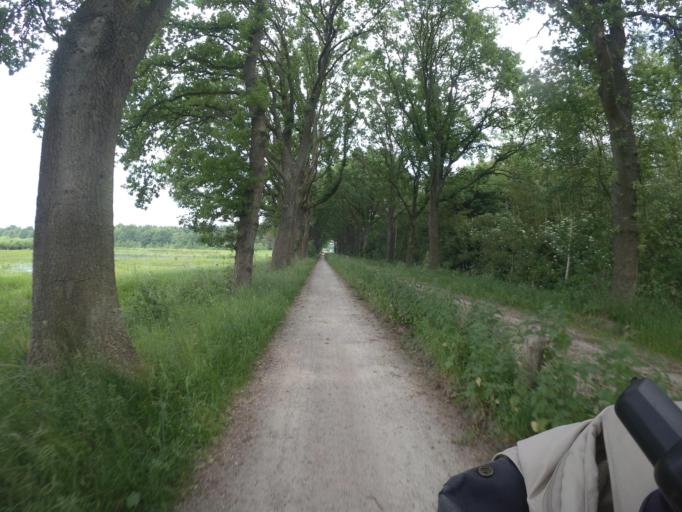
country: NL
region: Drenthe
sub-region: Gemeente Assen
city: Assen
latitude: 53.0111
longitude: 6.4382
